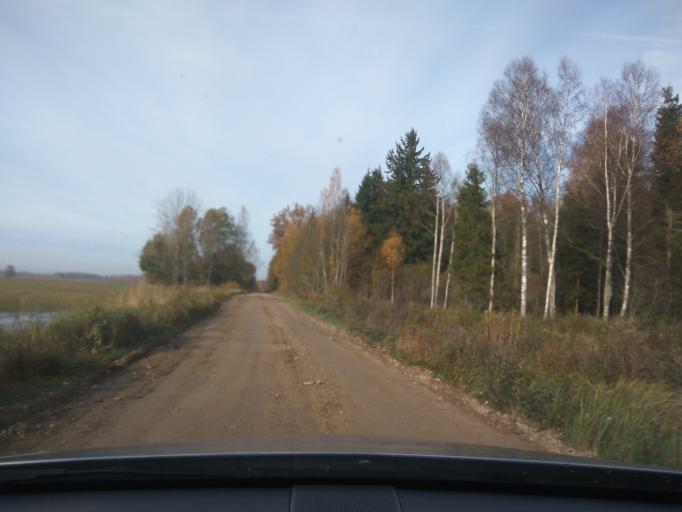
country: LV
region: Aizpute
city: Aizpute
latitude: 56.8428
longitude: 21.7130
